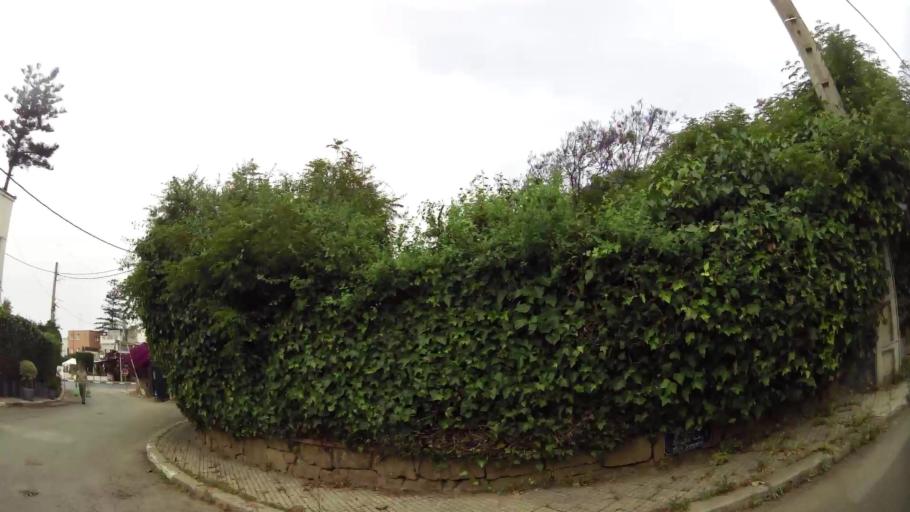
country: MA
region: Rabat-Sale-Zemmour-Zaer
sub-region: Rabat
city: Rabat
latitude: 34.0301
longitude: -6.8129
